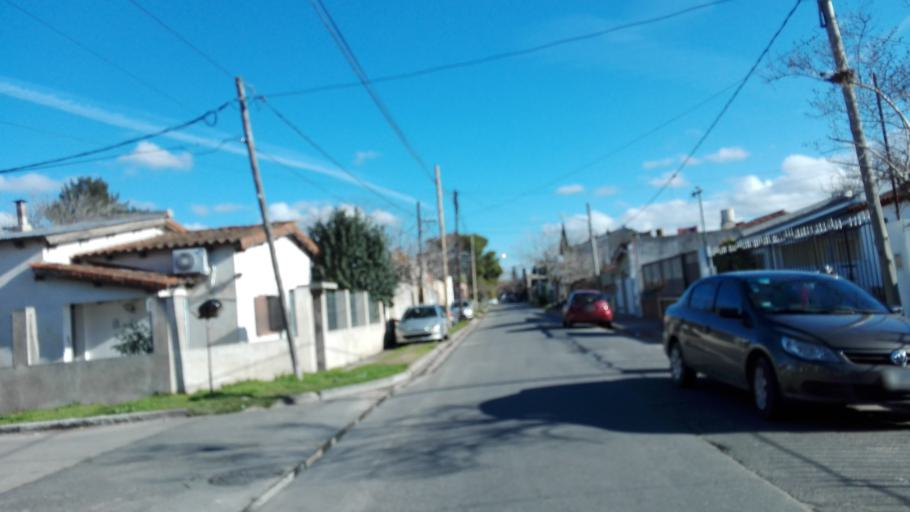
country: AR
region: Buenos Aires
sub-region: Partido de La Plata
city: La Plata
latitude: -34.8835
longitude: -57.9971
